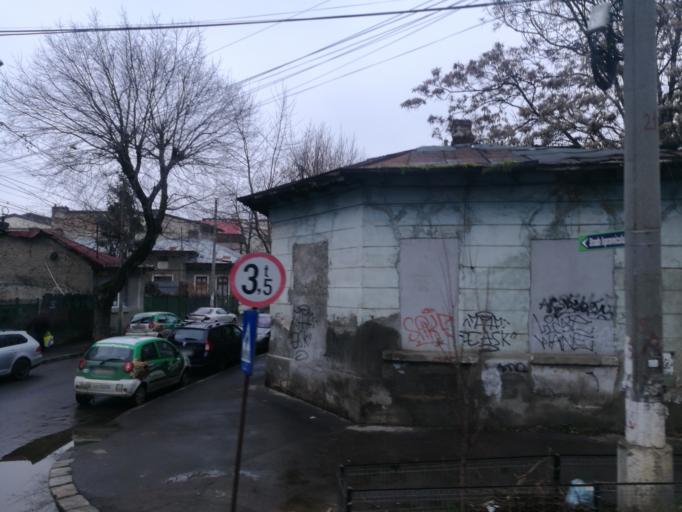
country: RO
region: Bucuresti
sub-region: Municipiul Bucuresti
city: Bucharest
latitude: 44.4573
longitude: 26.1205
